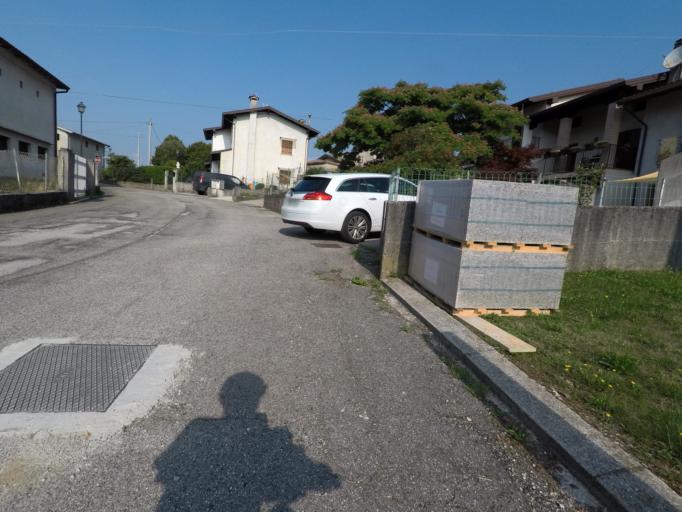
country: IT
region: Friuli Venezia Giulia
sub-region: Provincia di Pordenone
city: Meduno
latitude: 46.2026
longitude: 12.8307
